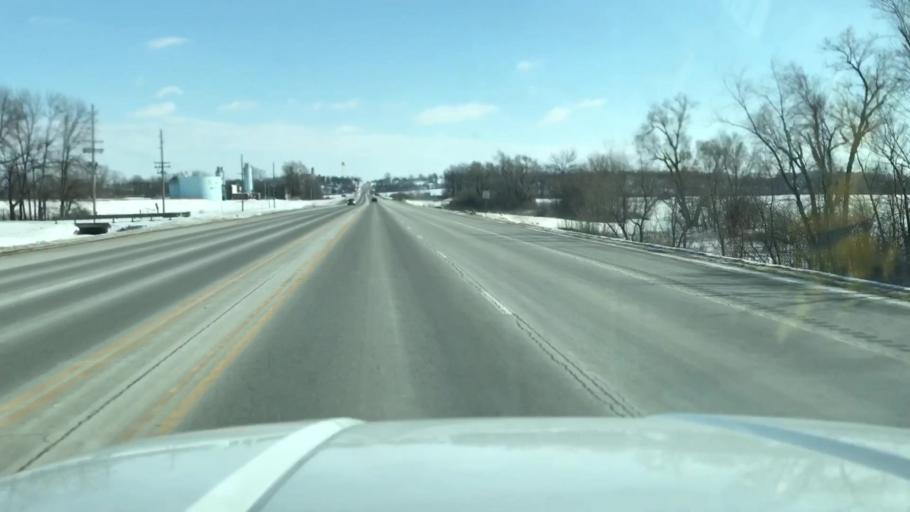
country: US
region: Missouri
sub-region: Nodaway County
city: Maryville
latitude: 40.3449
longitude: -94.8389
